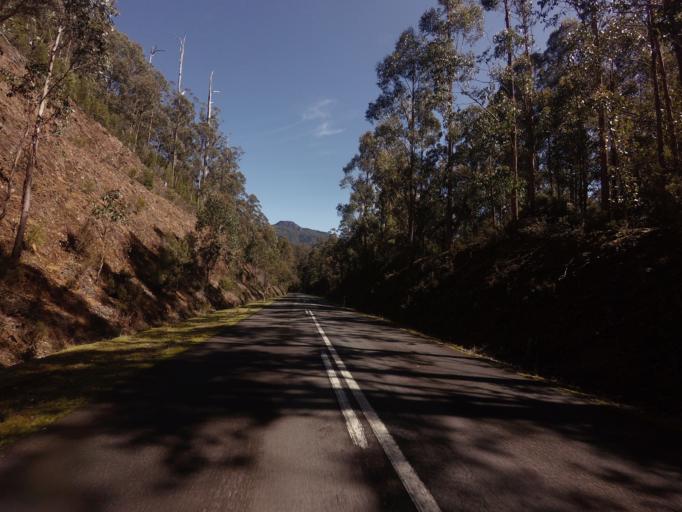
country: AU
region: Tasmania
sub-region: Derwent Valley
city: New Norfolk
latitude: -42.7427
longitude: 146.4983
